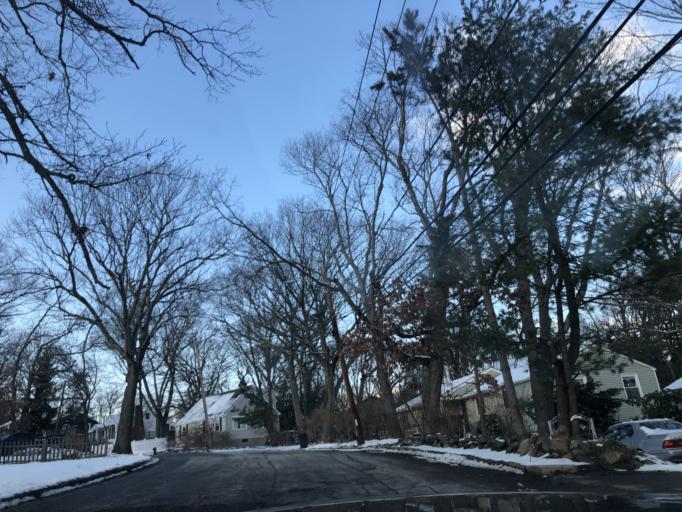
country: US
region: Massachusetts
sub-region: Middlesex County
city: Arlington
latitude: 42.4244
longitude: -71.1595
